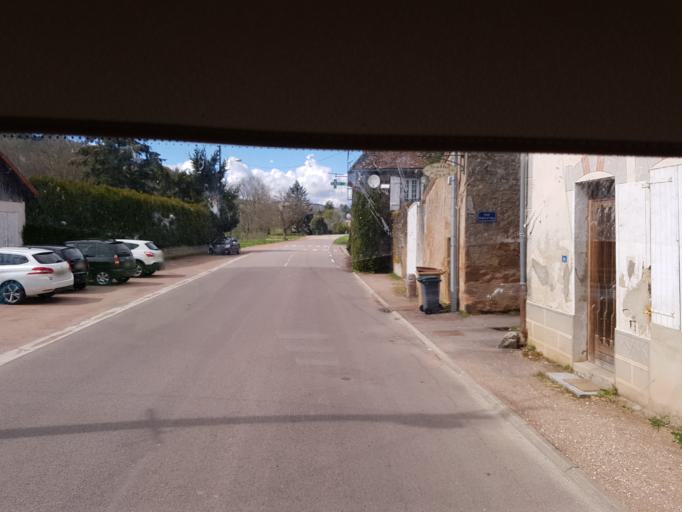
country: FR
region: Bourgogne
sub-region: Departement de Saone-et-Loire
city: Autun
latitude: 47.0831
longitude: 4.2438
